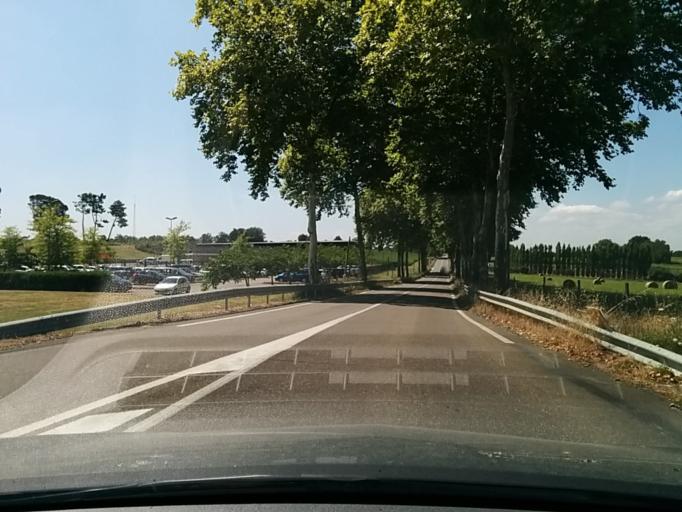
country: FR
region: Midi-Pyrenees
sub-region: Departement du Gers
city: Le Houga
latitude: 43.7863
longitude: -0.2157
